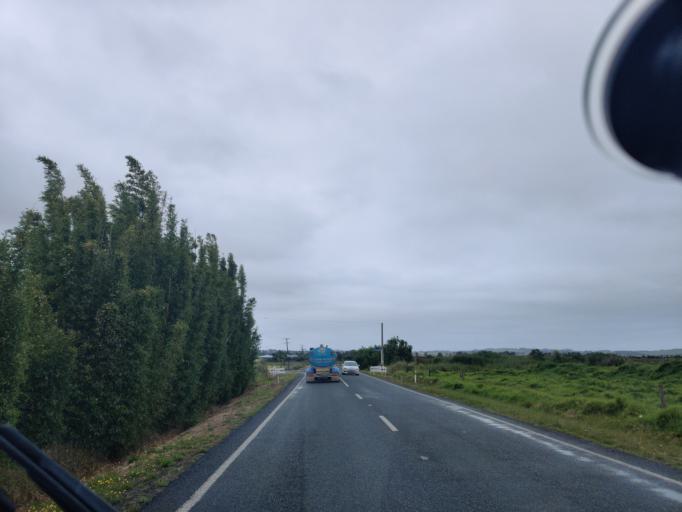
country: NZ
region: Northland
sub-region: Kaipara District
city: Dargaville
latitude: -36.0857
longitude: 173.9826
